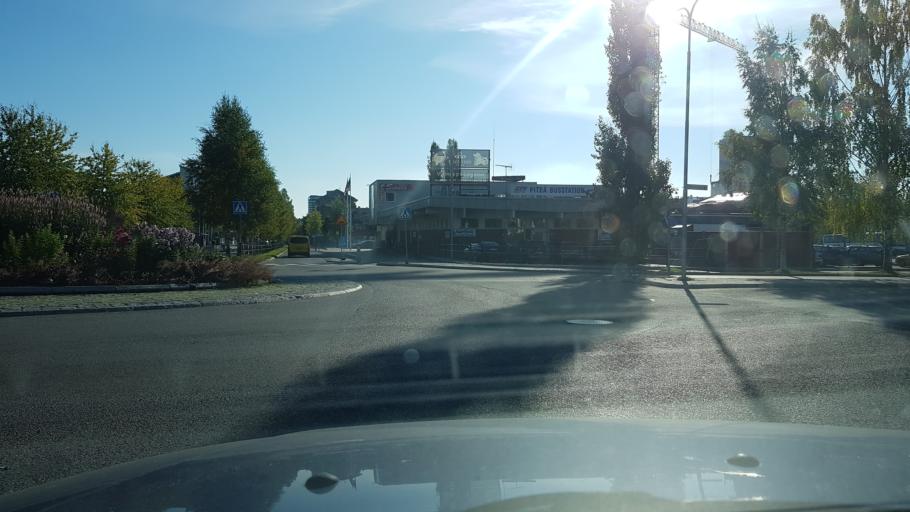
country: SE
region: Norrbotten
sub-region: Pitea Kommun
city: Pitea
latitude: 65.3204
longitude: 21.4739
